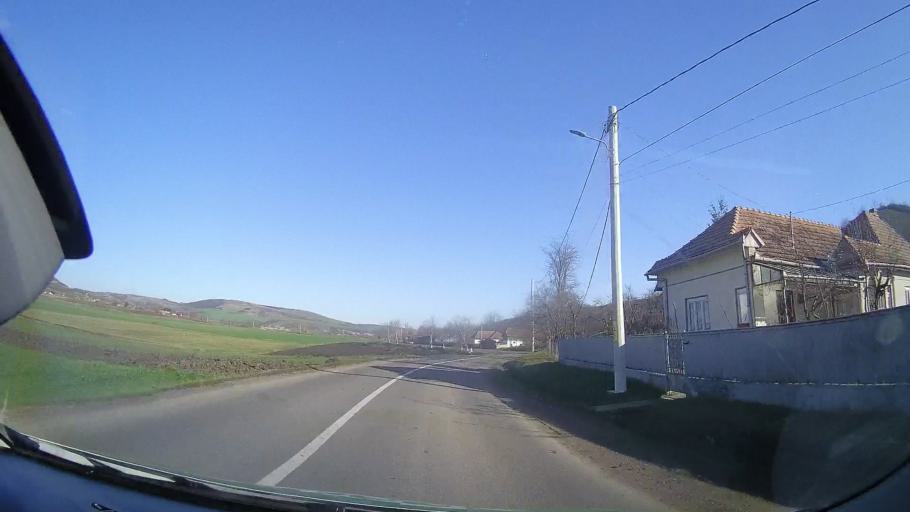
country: RO
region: Mures
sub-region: Comuna Band
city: Band
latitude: 46.5753
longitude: 24.3484
